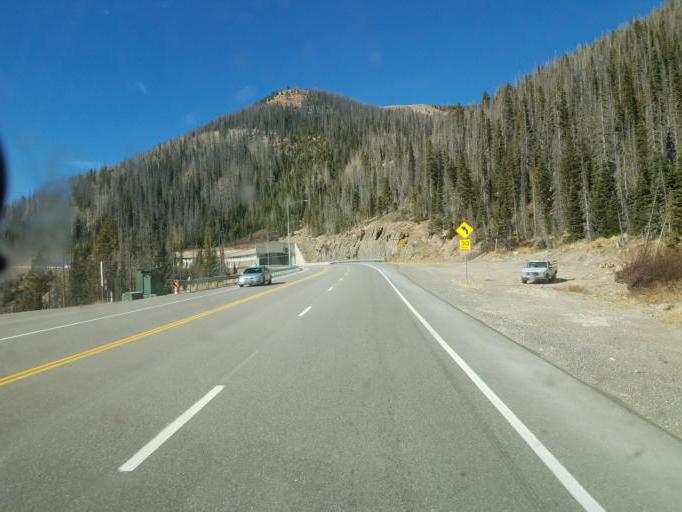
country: US
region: Colorado
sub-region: Archuleta County
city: Pagosa Springs
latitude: 37.4791
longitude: -106.7768
